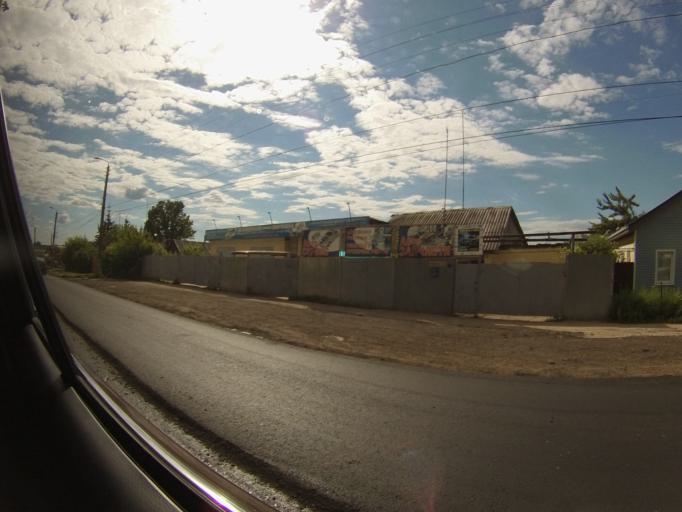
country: RU
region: Orjol
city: Mtsensk
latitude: 53.2876
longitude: 36.5817
